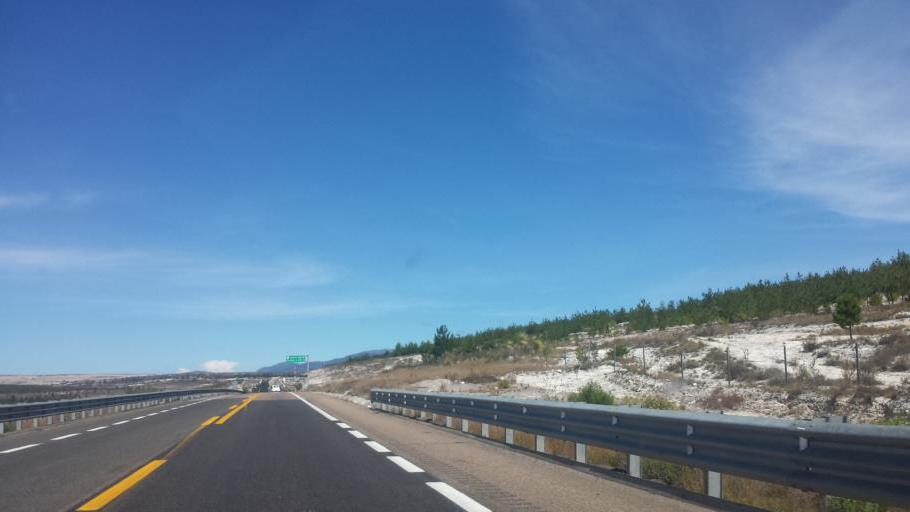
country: MX
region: Oaxaca
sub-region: Villa Tejupam de la Union
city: Villa Tejupam de la Union
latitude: 17.8591
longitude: -97.3778
